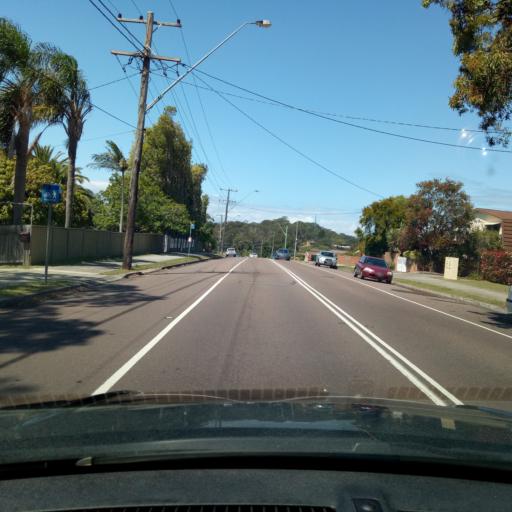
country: AU
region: New South Wales
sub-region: Wyong Shire
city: Tumbi Vmbi
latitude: -33.3736
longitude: 151.4535
